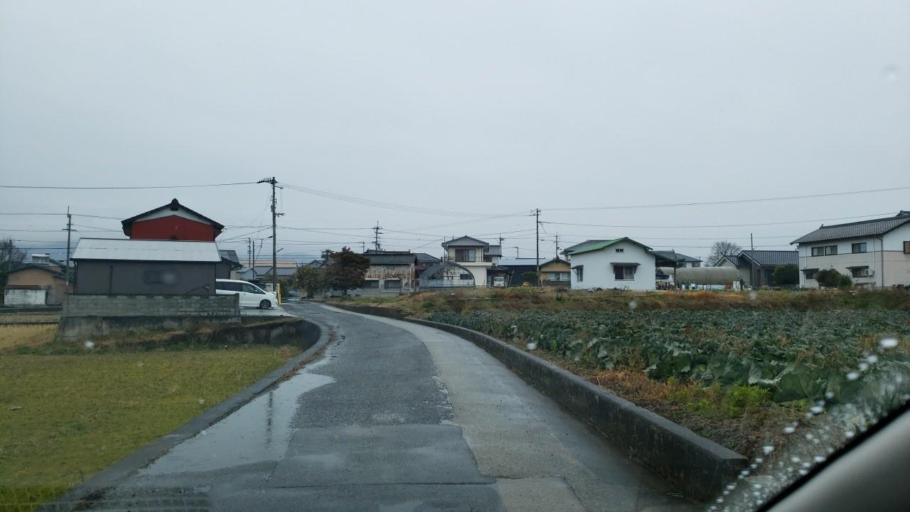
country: JP
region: Tokushima
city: Kamojimacho-jogejima
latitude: 34.0785
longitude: 134.2566
